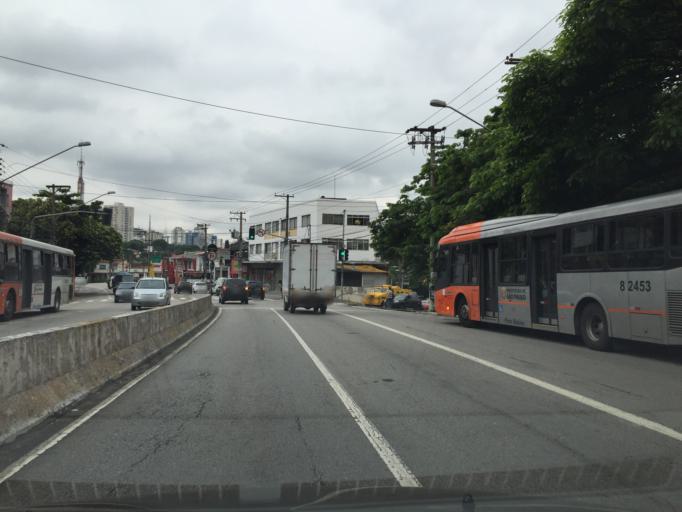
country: BR
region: Sao Paulo
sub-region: Sao Paulo
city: Sao Paulo
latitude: -23.5473
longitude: -46.6897
